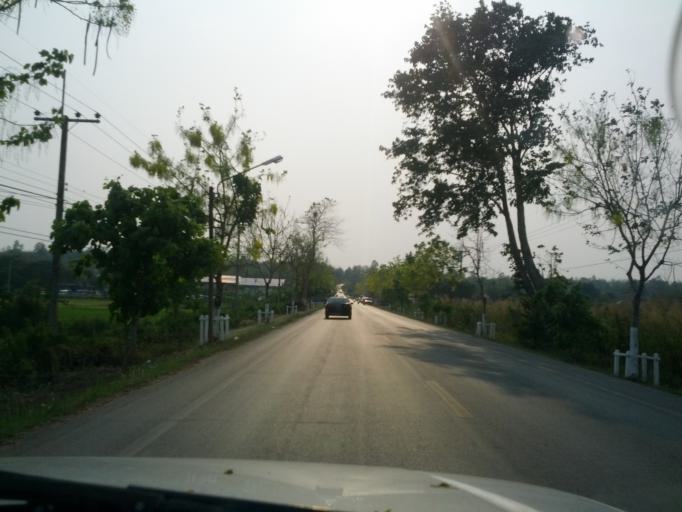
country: TH
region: Chiang Mai
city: Mae Taeng
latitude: 19.1441
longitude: 98.9872
